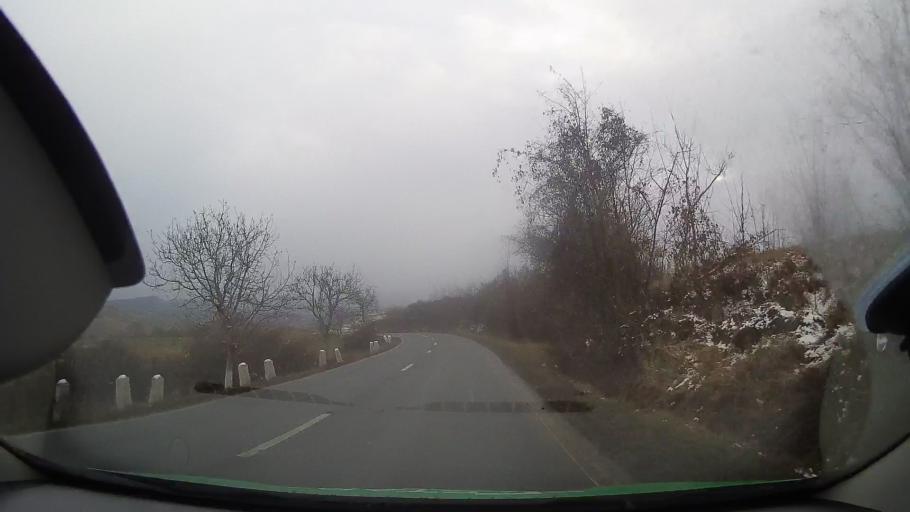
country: RO
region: Sibiu
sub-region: Comuna Blajel
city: Blajel
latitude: 46.2462
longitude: 24.3002
